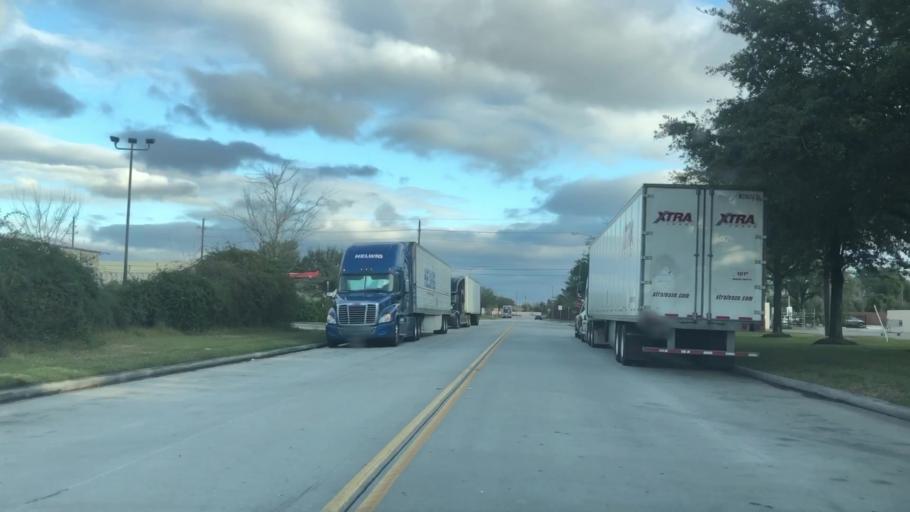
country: US
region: Texas
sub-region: Harris County
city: Aldine
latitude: 29.9203
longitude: -95.4161
